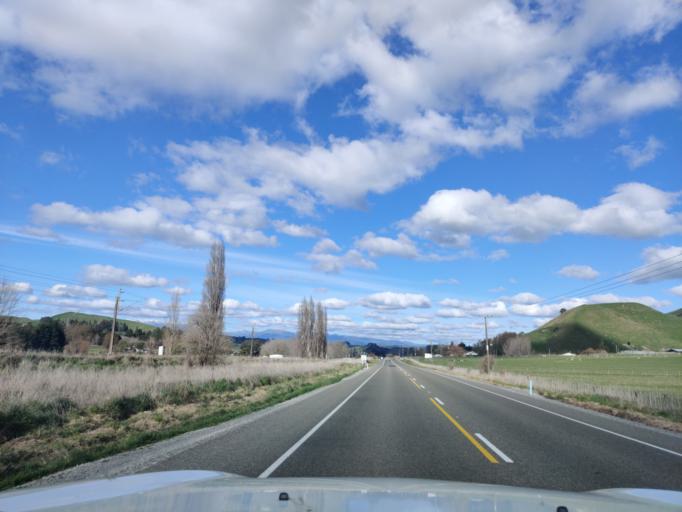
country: NZ
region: Manawatu-Wanganui
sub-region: Ruapehu District
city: Waiouru
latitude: -39.7006
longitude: 175.8279
